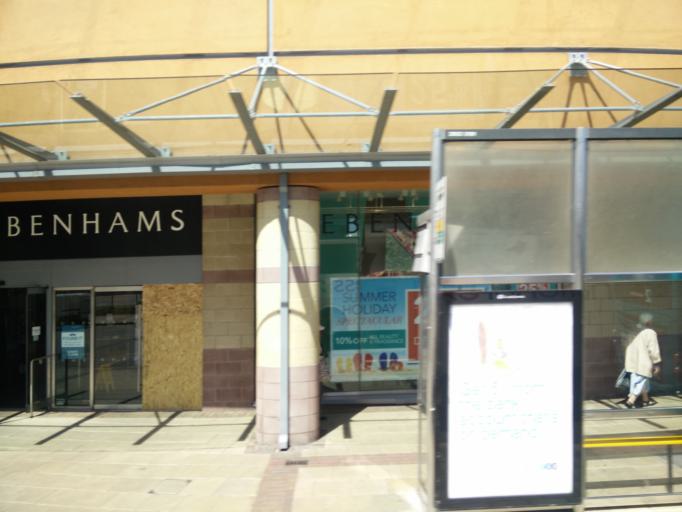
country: GB
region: England
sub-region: Hertfordshire
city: Hemel Hempstead
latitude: 51.7470
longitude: -0.4740
